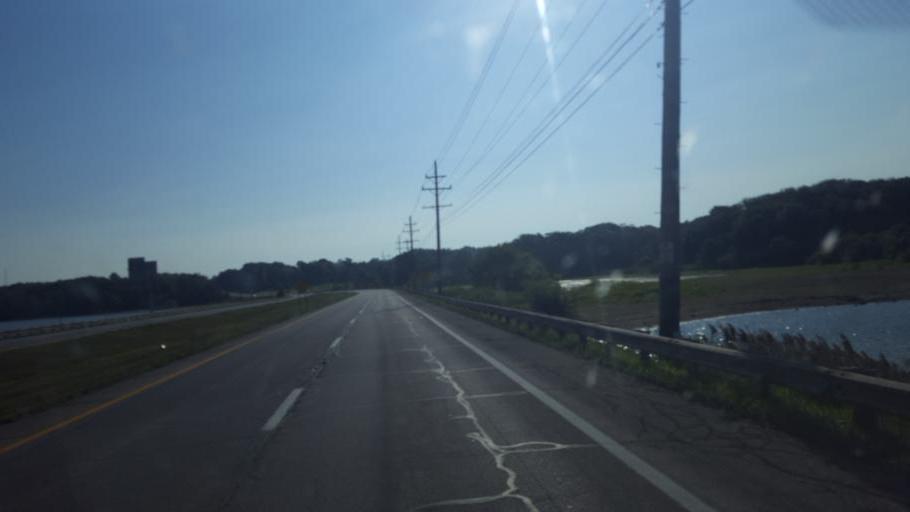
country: US
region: Ohio
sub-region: Portage County
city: Hiram
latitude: 41.3834
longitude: -81.1964
